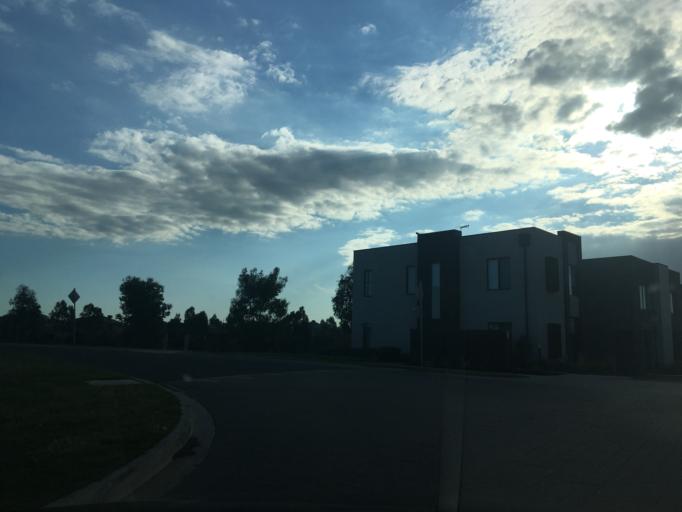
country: AU
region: Victoria
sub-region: Wyndham
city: Hoppers Crossing
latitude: -37.8783
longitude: 144.7238
